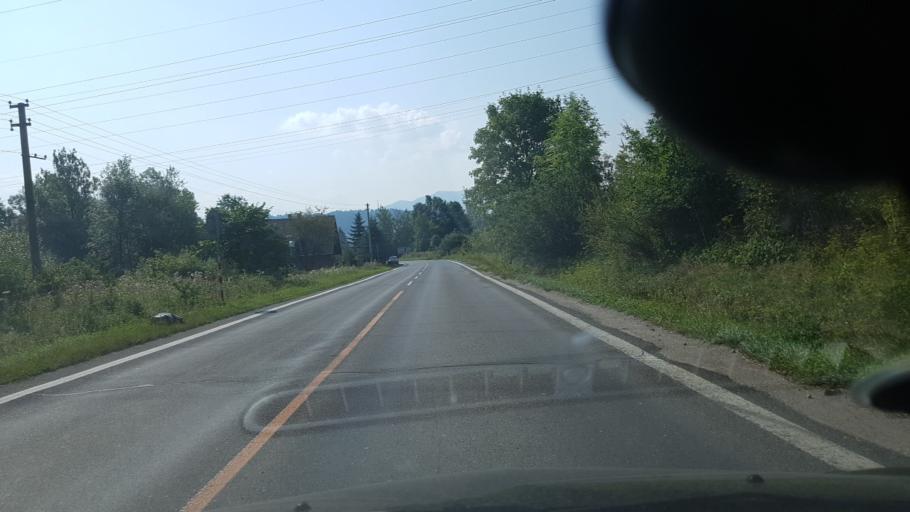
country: SK
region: Zilinsky
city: Ruzomberok
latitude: 49.1053
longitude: 19.3017
